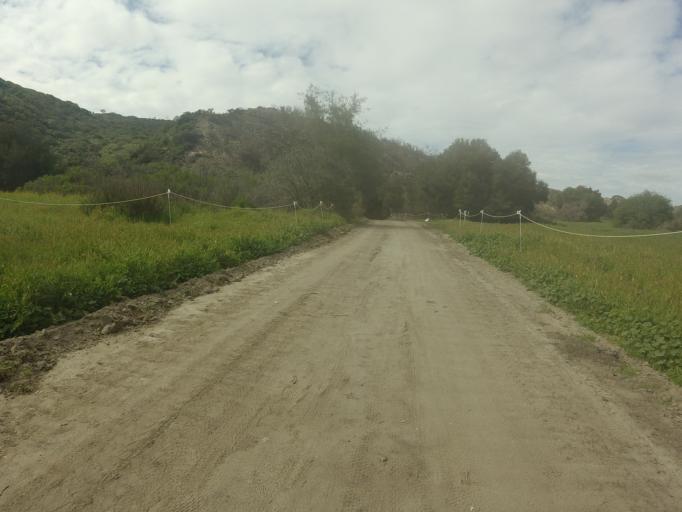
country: US
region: California
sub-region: Orange County
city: Aliso Viejo
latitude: 33.5469
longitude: -117.7406
